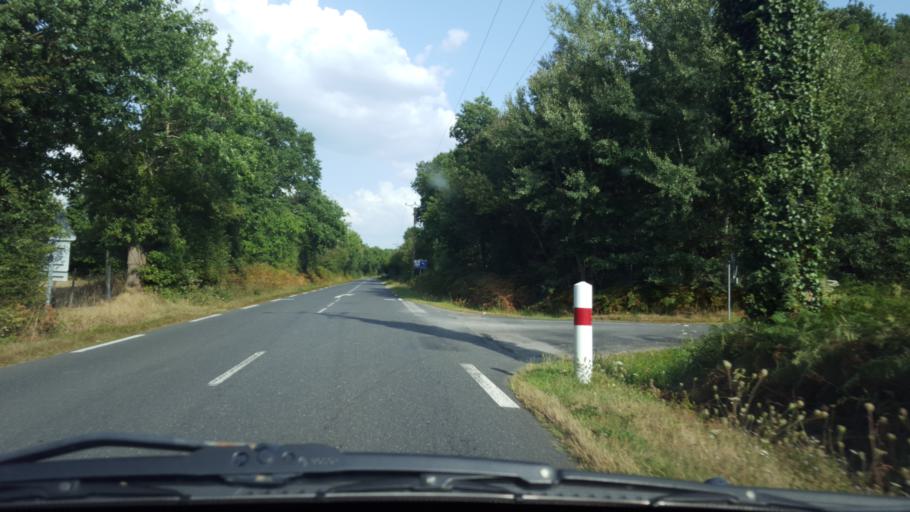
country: FR
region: Pays de la Loire
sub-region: Departement de la Loire-Atlantique
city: Geneston
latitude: 47.0602
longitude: -1.5356
